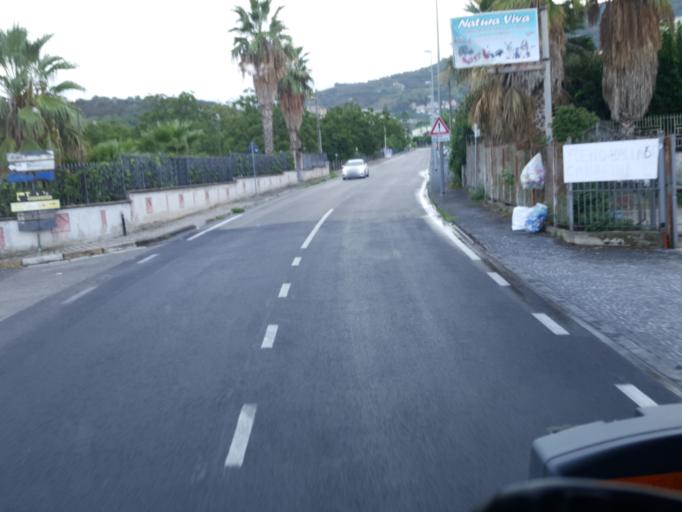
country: IT
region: Campania
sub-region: Provincia di Napoli
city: Carbonara di Nola
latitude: 40.8815
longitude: 14.5719
